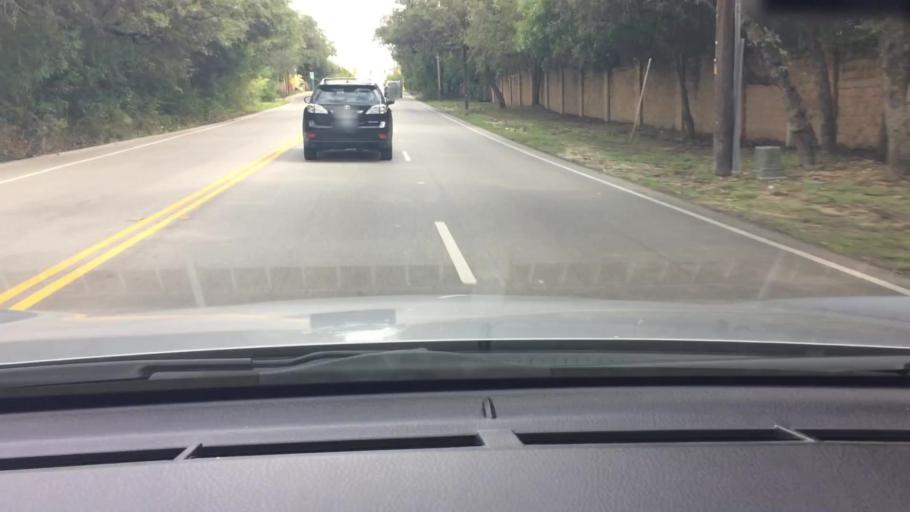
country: US
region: Texas
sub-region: Bexar County
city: Castle Hills
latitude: 29.5456
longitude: -98.5338
